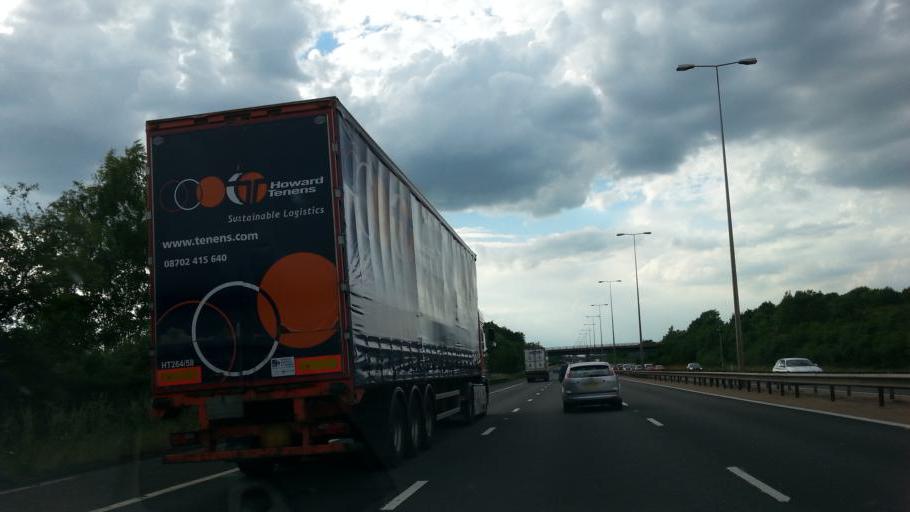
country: GB
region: England
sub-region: Worcestershire
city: Upton upon Severn
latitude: 52.0745
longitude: -2.1652
